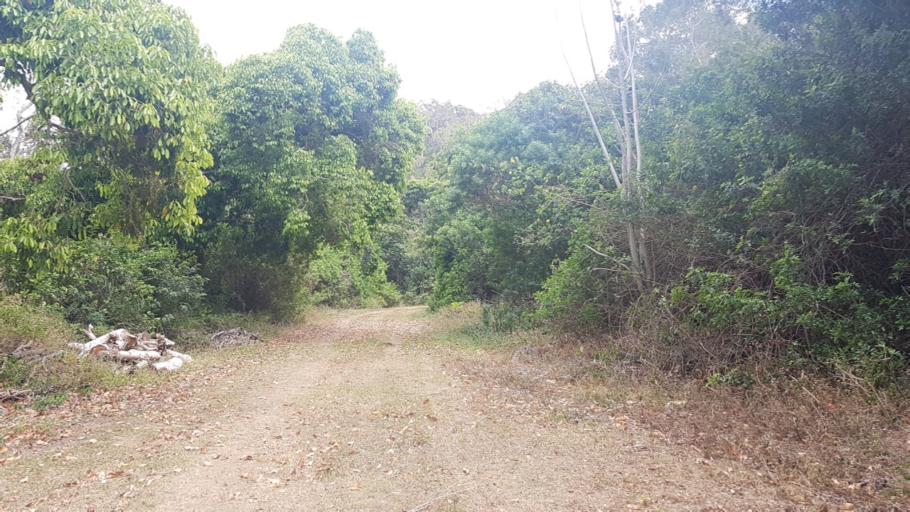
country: NC
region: South Province
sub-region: Dumbea
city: Dumbea
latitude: -22.1772
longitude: 166.4767
